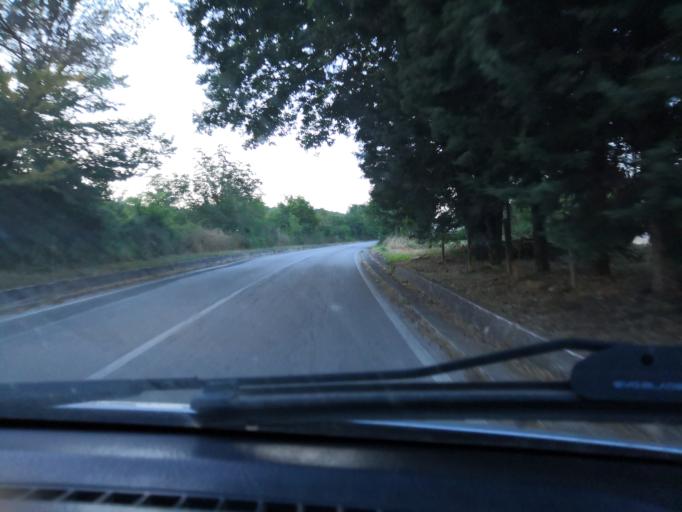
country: IT
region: Molise
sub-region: Provincia di Campobasso
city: Jelsi
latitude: 41.5119
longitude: 14.7846
